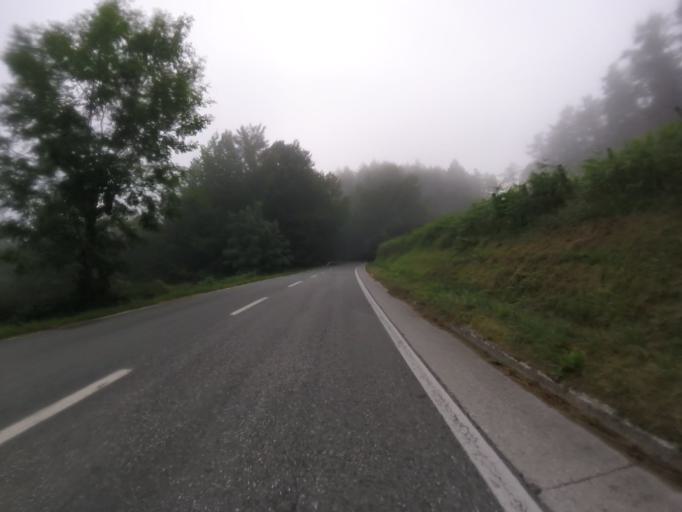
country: ES
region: Navarre
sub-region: Provincia de Navarra
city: Leitza
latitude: 43.0841
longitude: -1.8753
